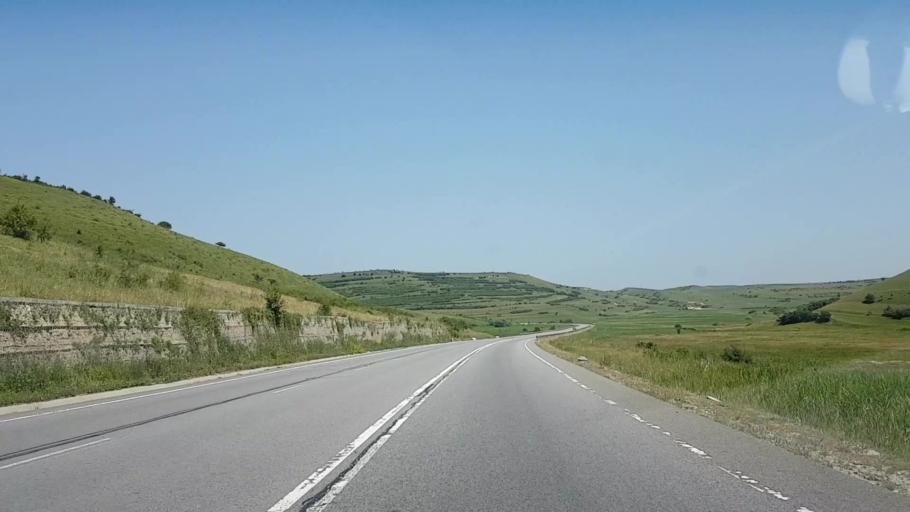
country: RO
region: Cluj
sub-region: Comuna Feleacu
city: Gheorghieni
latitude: 46.7330
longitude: 23.6918
